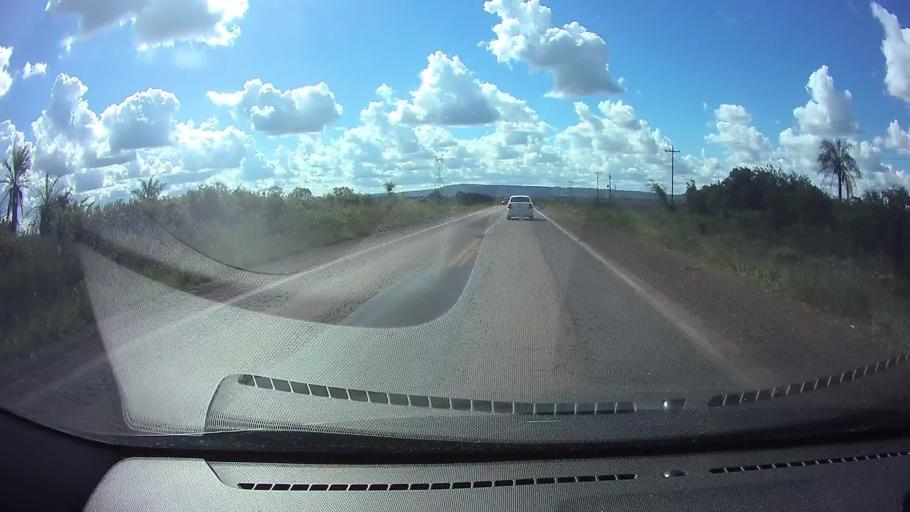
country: PY
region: Paraguari
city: Sapucai
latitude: -25.7297
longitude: -56.8218
